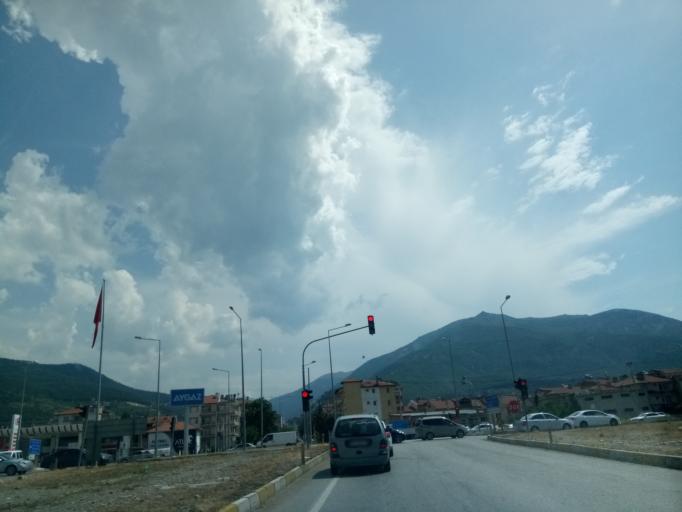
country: TR
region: Afyonkarahisar
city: Cay
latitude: 38.5976
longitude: 31.0288
